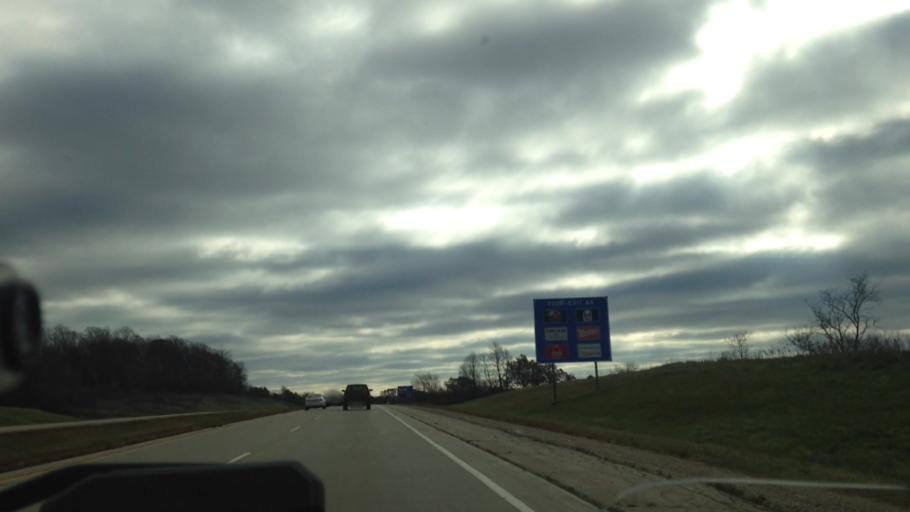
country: US
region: Wisconsin
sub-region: Washington County
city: West Bend
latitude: 43.4069
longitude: -88.2002
